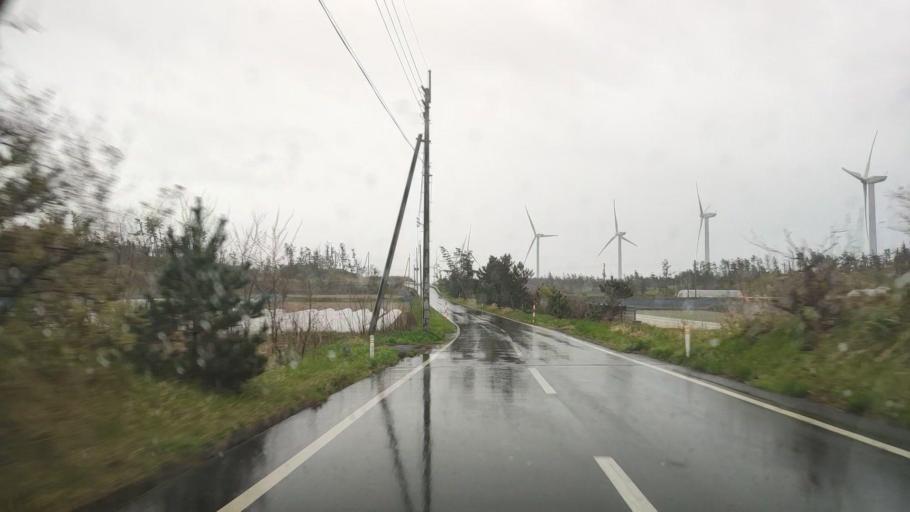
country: JP
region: Akita
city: Noshiromachi
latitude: 40.0785
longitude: 139.9533
